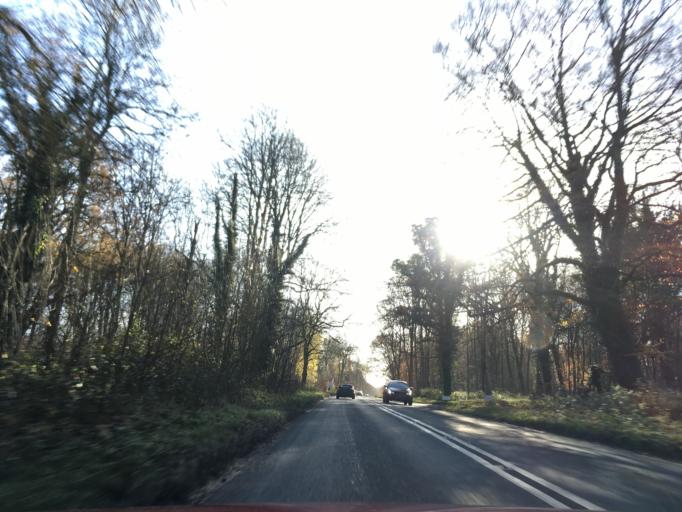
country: GB
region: England
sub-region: Wiltshire
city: Mildenhall
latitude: 51.3896
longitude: -1.6942
